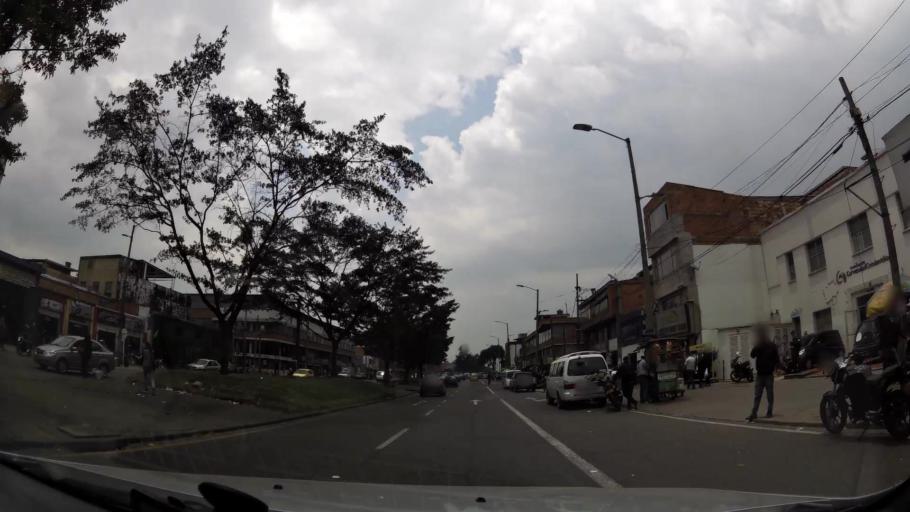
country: CO
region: Bogota D.C.
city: Bogota
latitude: 4.5914
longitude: -74.1104
